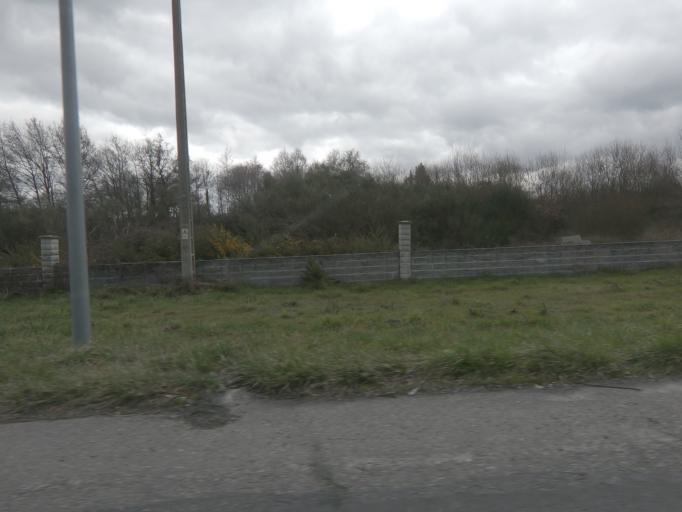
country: ES
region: Galicia
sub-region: Provincia de Ourense
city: Allariz
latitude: 42.1912
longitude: -7.7894
